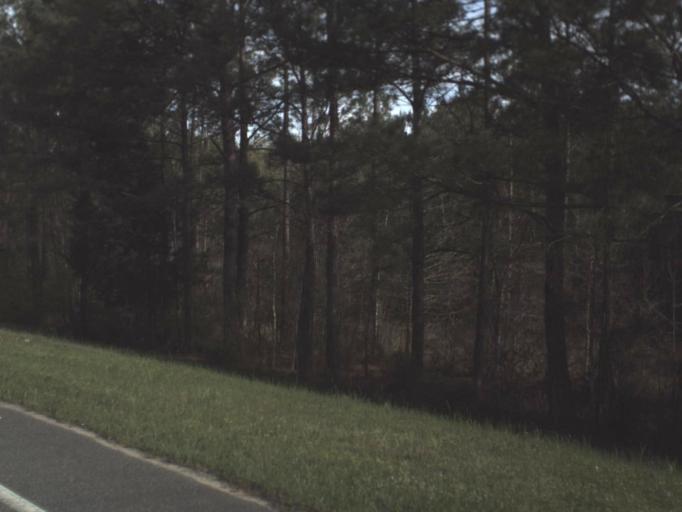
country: US
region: Florida
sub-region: Holmes County
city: Bonifay
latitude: 30.7789
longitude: -85.6201
